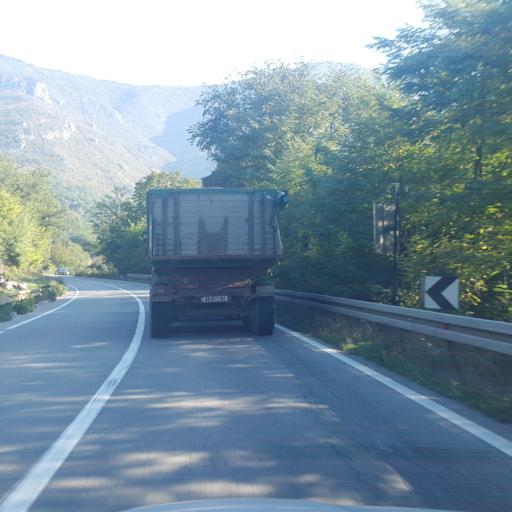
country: RS
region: Central Serbia
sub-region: Nisavski Okrug
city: Svrljig
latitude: 43.3303
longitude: 22.1154
